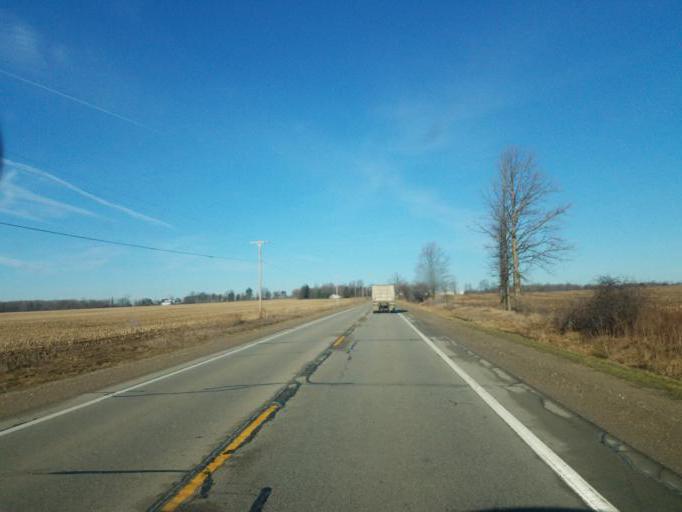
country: US
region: Michigan
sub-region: Gratiot County
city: Alma
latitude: 43.4082
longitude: -84.7077
